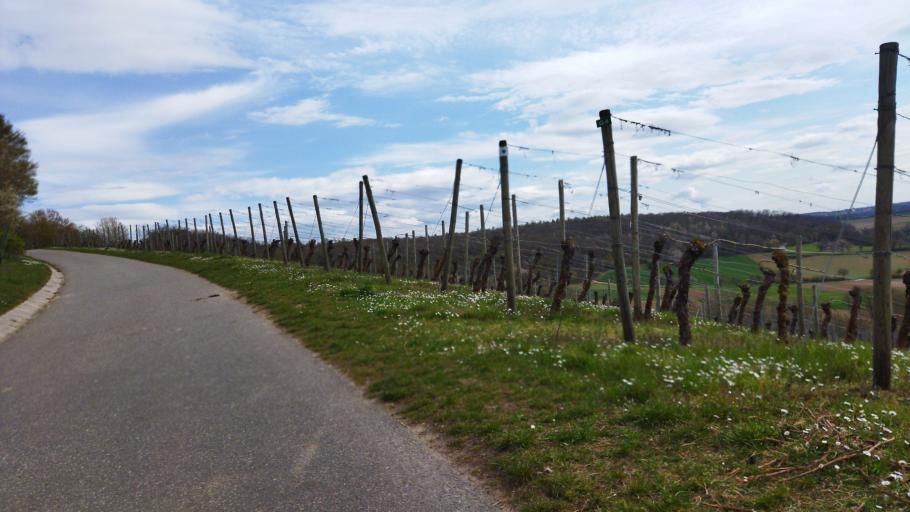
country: DE
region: Baden-Wuerttemberg
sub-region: Regierungsbezirk Stuttgart
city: Gundelsheim
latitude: 49.2822
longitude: 9.1767
